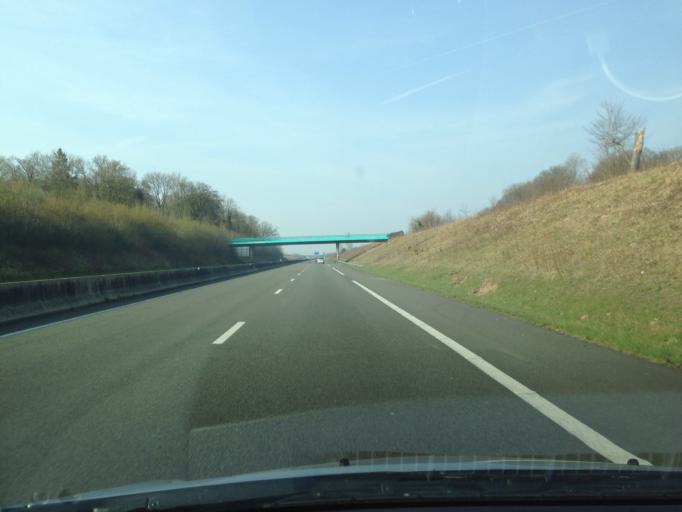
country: FR
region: Picardie
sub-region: Departement de la Somme
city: Nouvion
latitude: 50.2412
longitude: 1.7512
